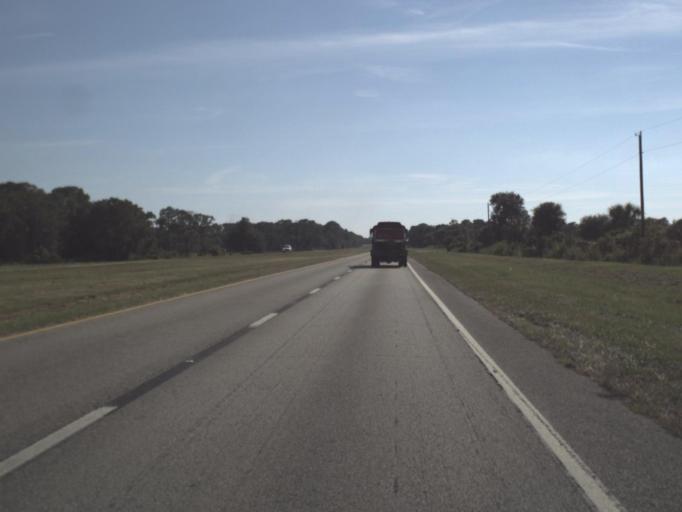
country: US
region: Florida
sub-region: Highlands County
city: Placid Lakes
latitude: 27.0494
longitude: -81.3402
